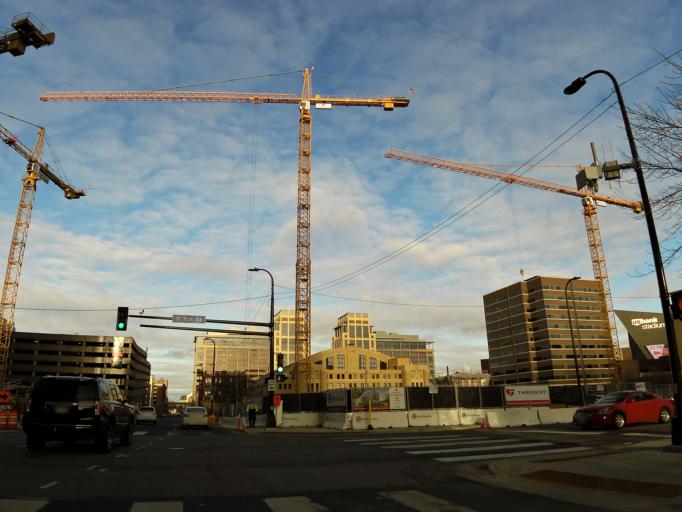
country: US
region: Minnesota
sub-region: Hennepin County
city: Minneapolis
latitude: 44.9739
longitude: -93.2656
